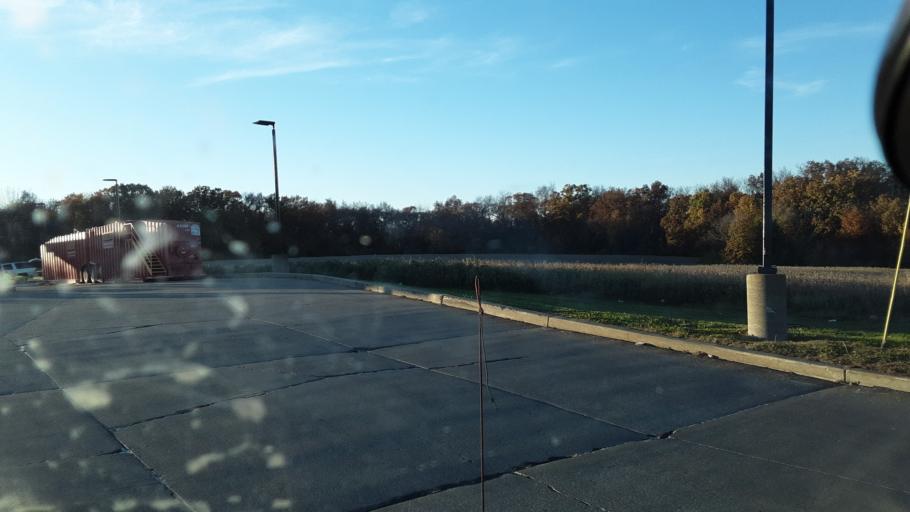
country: US
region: Missouri
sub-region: Warren County
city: Wright City
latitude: 38.8188
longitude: -90.9522
